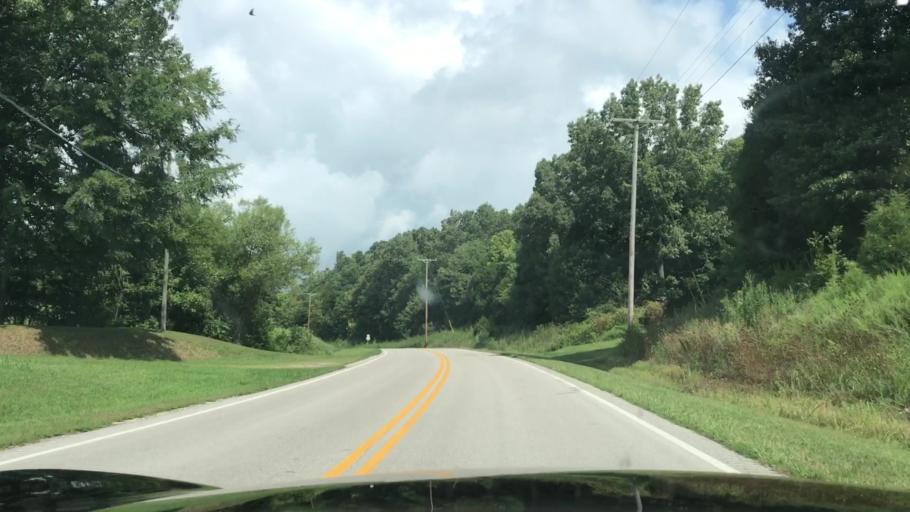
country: US
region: Kentucky
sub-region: Ohio County
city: Oak Grove
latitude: 37.2051
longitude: -86.8883
